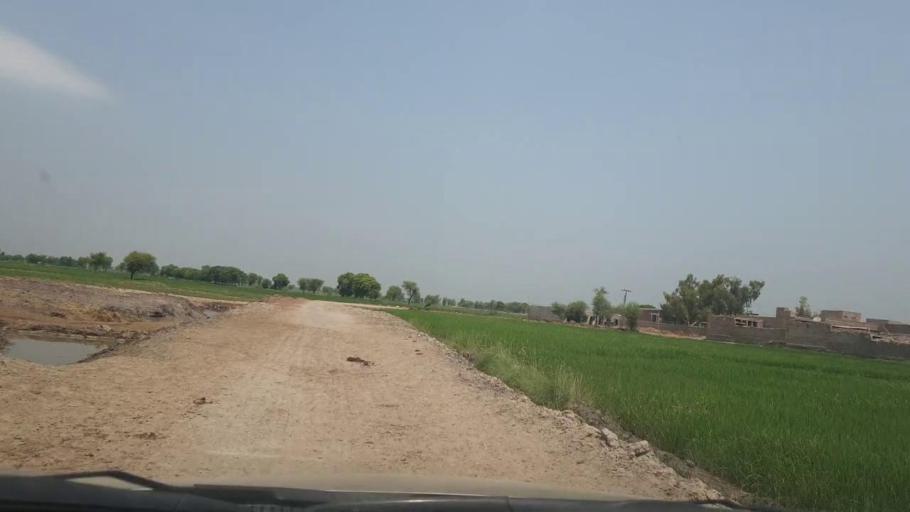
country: PK
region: Sindh
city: Ratodero
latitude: 27.7286
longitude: 68.2949
